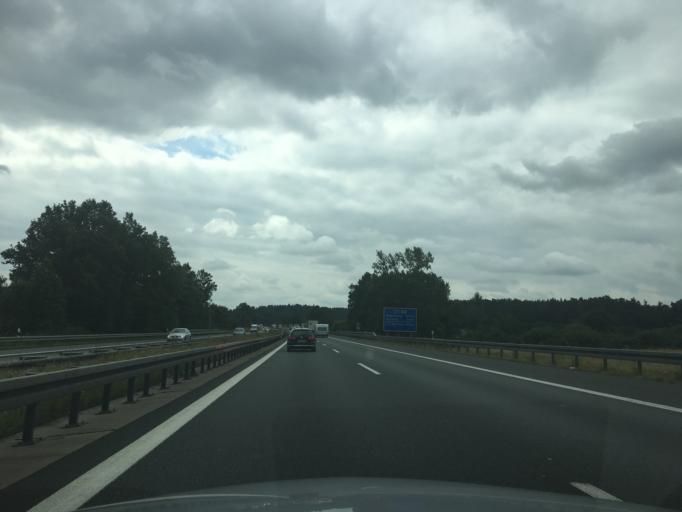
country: DE
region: Bavaria
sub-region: Regierungsbezirk Mittelfranken
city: Hessdorf
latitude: 49.6259
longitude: 10.9190
